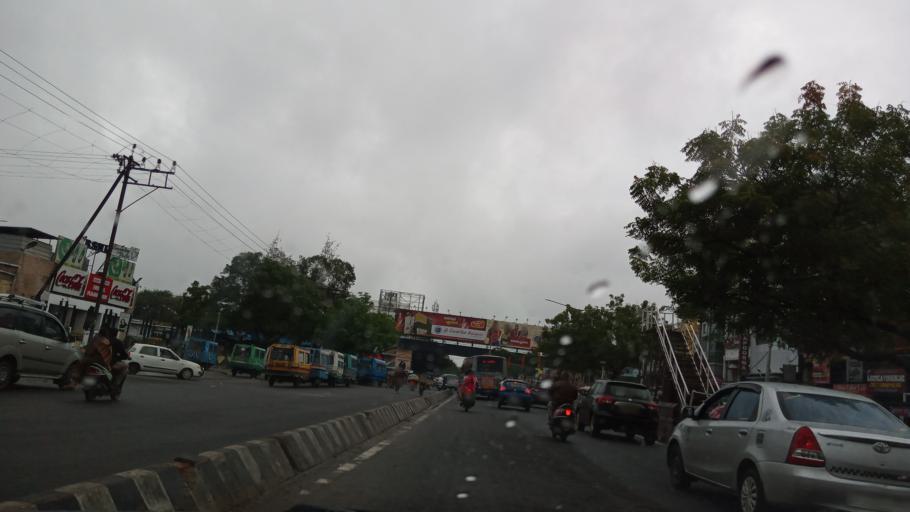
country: IN
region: Pondicherry
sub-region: Puducherry
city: Puducherry
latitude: 11.9322
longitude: 79.8150
